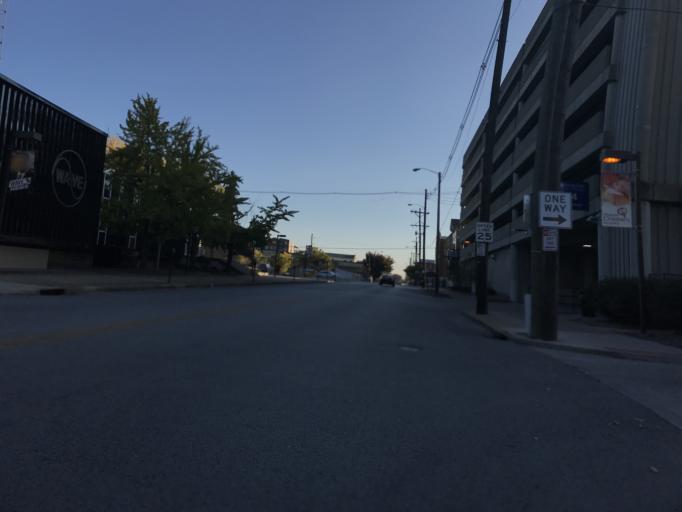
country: US
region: Kentucky
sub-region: Jefferson County
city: Louisville
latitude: 38.2448
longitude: -85.7499
